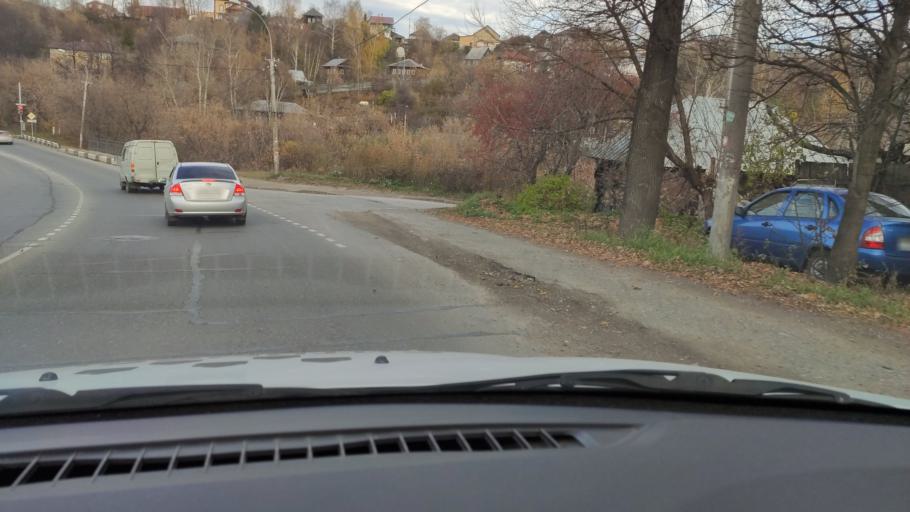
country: RU
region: Perm
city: Perm
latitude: 58.0398
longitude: 56.3277
